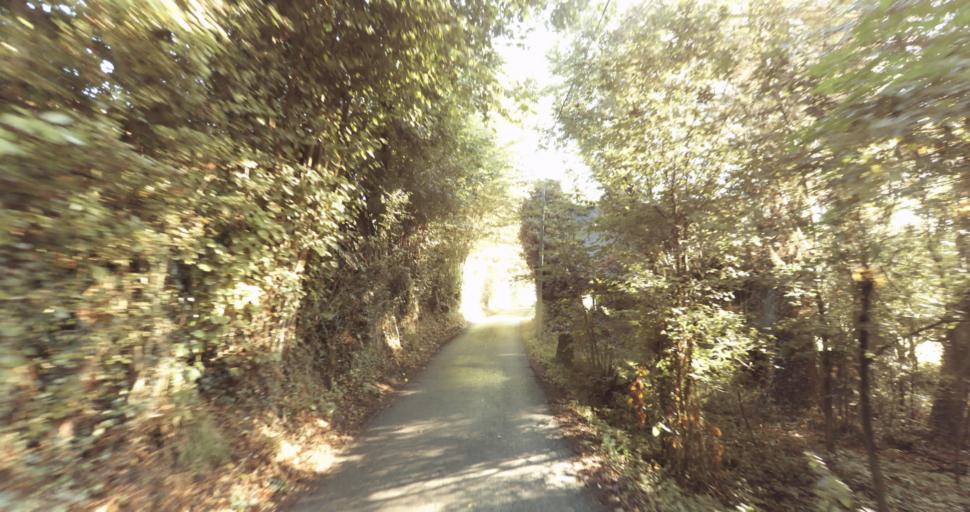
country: FR
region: Lower Normandy
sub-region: Departement de l'Orne
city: Vimoutiers
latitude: 48.9229
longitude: 0.1751
